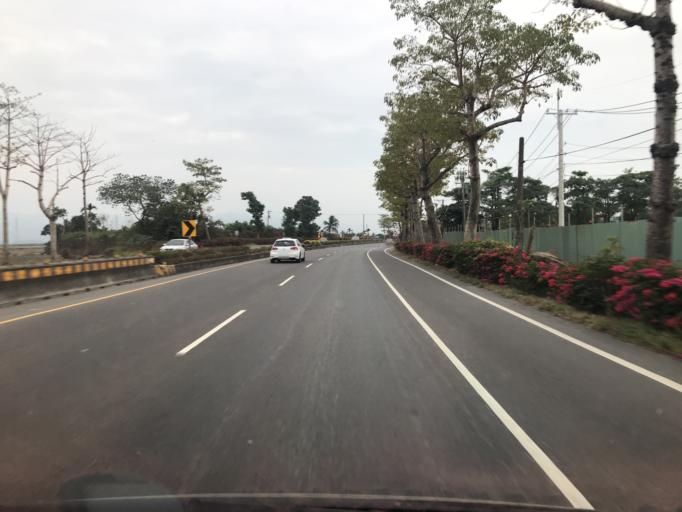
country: TW
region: Taiwan
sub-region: Pingtung
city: Pingtung
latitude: 22.4212
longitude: 120.5821
